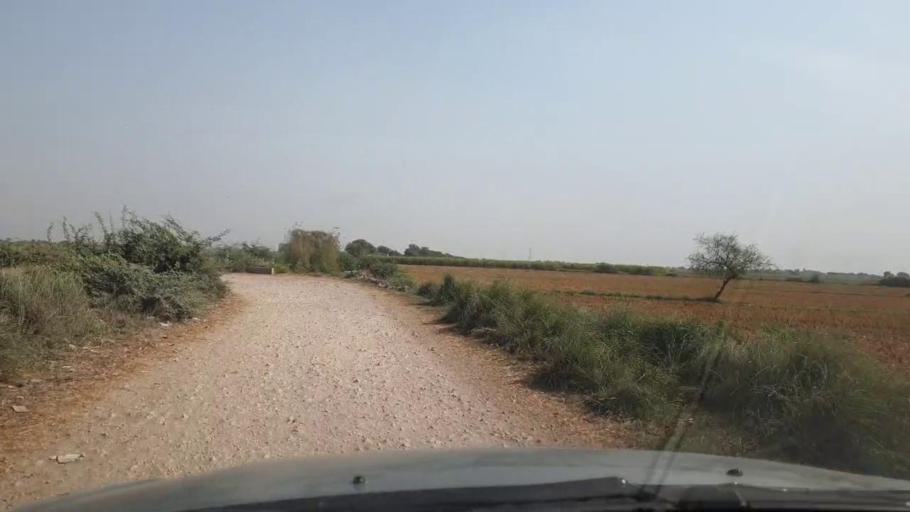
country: PK
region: Sindh
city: Bulri
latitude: 24.9212
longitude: 68.3531
